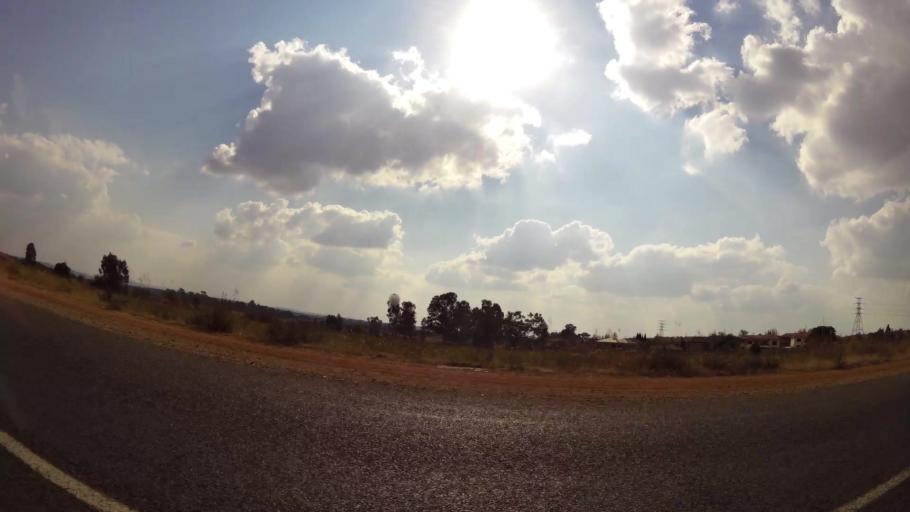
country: ZA
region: Gauteng
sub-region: City of Tshwane Metropolitan Municipality
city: Centurion
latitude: -25.8632
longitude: 28.2402
